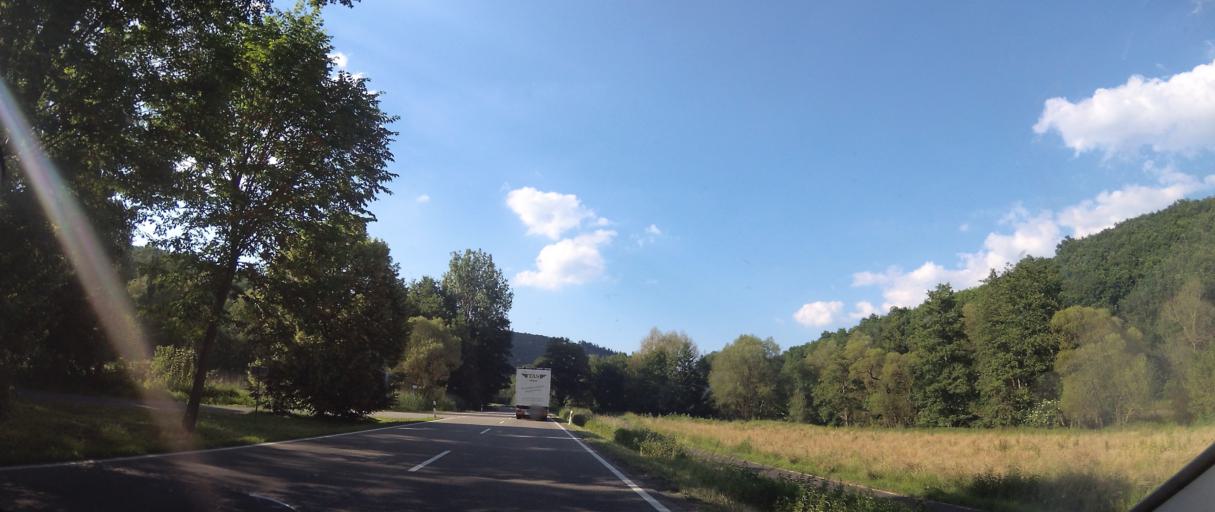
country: DE
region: Rheinland-Pfalz
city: Kalkofen
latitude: 49.7433
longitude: 7.8207
